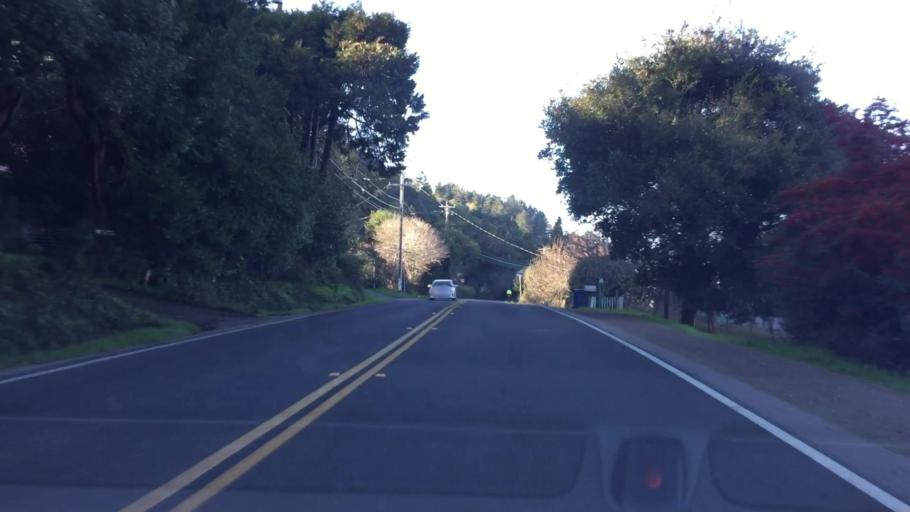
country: US
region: California
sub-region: Marin County
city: Inverness
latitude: 38.0728
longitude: -122.8270
